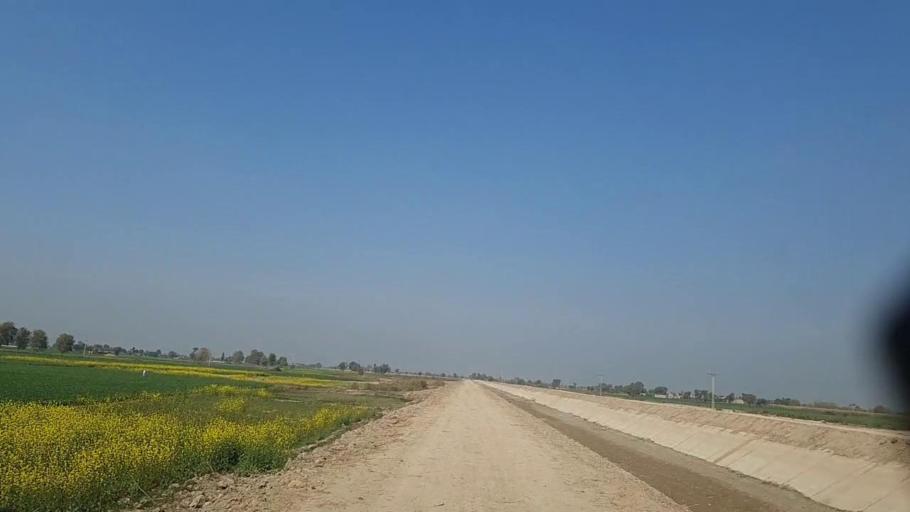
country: PK
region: Sindh
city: Sakrand
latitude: 26.1549
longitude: 68.3291
